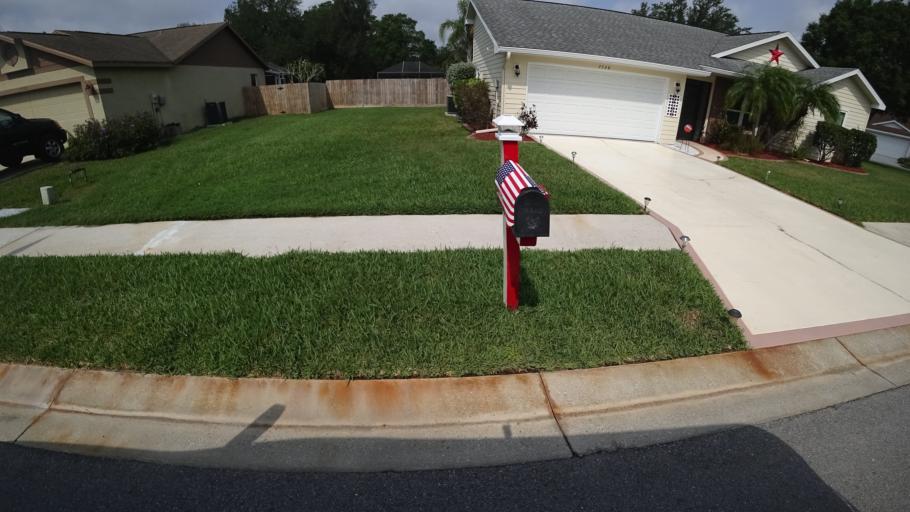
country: US
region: Florida
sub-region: Sarasota County
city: North Sarasota
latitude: 27.4019
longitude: -82.5200
